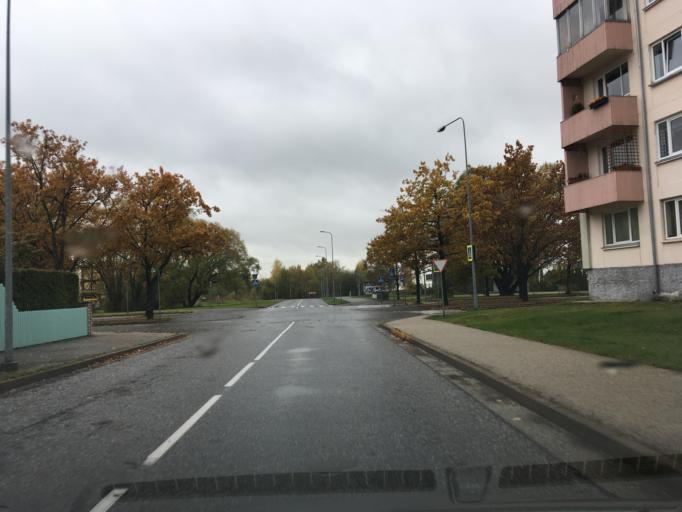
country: EE
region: Paernumaa
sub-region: Paernu linn
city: Parnu
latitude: 58.3742
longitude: 24.5162
